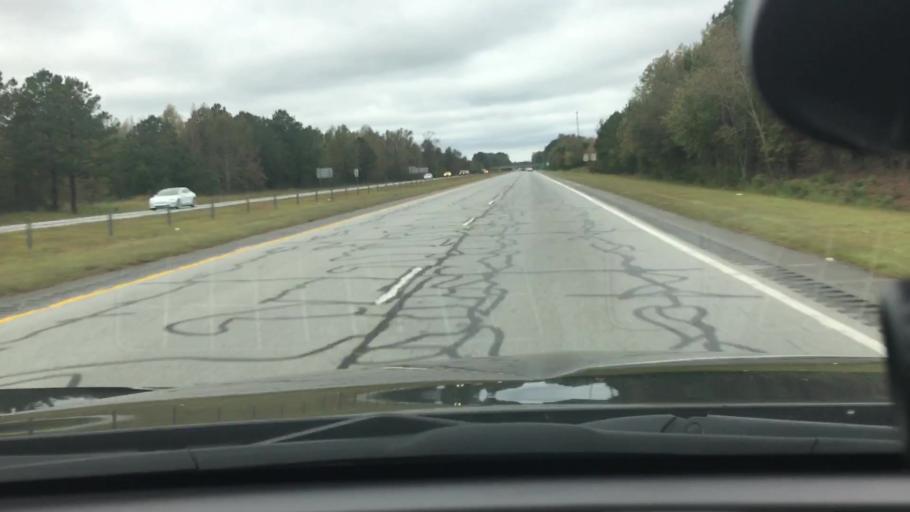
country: US
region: North Carolina
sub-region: Pitt County
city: Farmville
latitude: 35.6031
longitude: -77.5651
